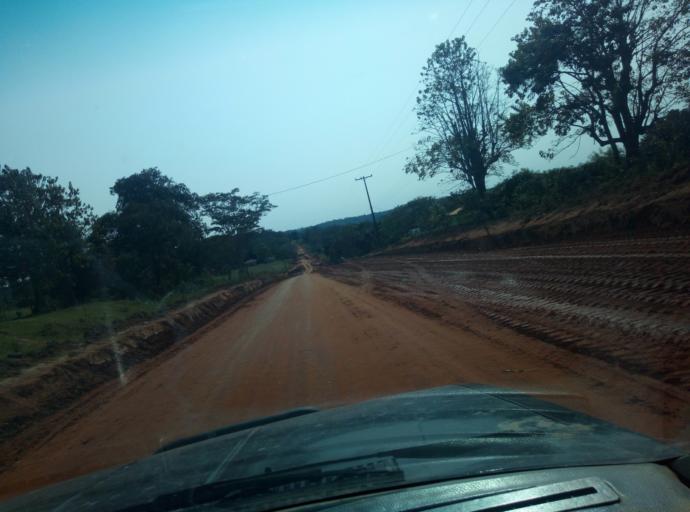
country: PY
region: Caaguazu
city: Carayao
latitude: -25.3131
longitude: -56.3267
